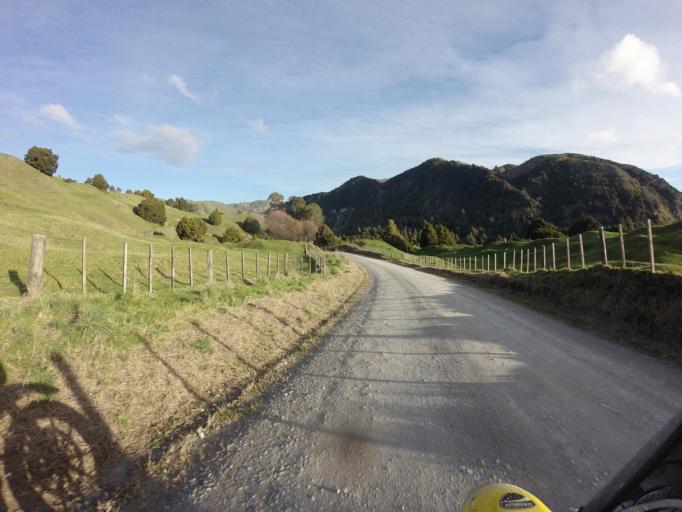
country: NZ
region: Hawke's Bay
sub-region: Wairoa District
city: Wairoa
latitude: -38.7264
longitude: 177.5879
